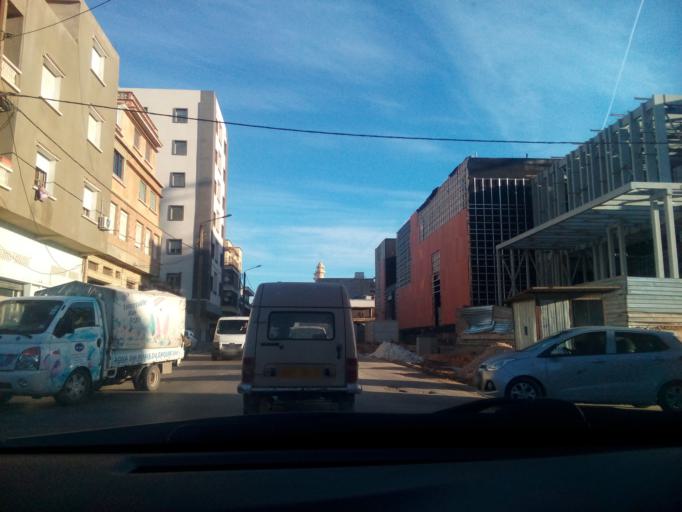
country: DZ
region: Oran
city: Oran
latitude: 35.6784
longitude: -0.6608
